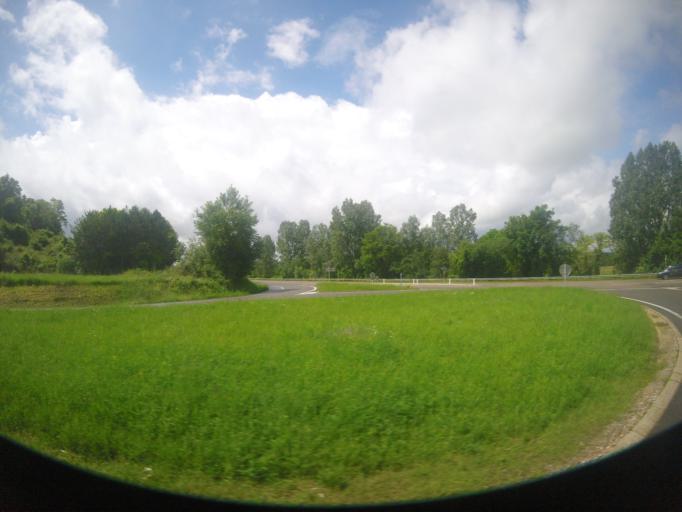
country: FR
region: Lorraine
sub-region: Departement de la Meuse
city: Dugny-sur-Meuse
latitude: 49.1117
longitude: 5.4132
